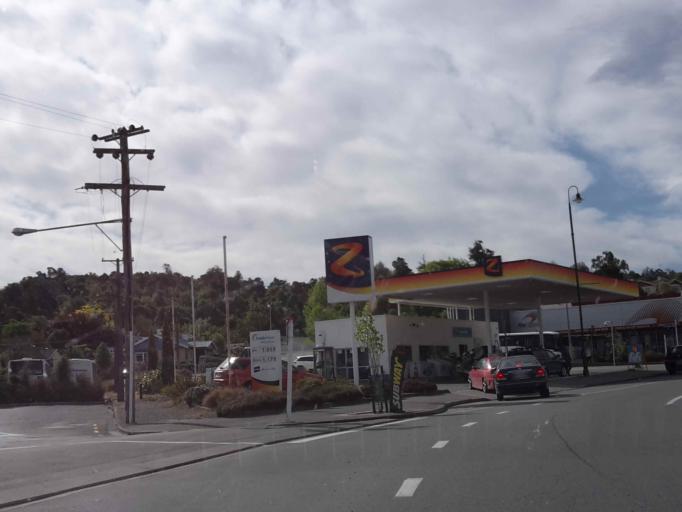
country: NZ
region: Canterbury
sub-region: Timaru District
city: Pleasant Point
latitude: -44.0904
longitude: 171.2430
